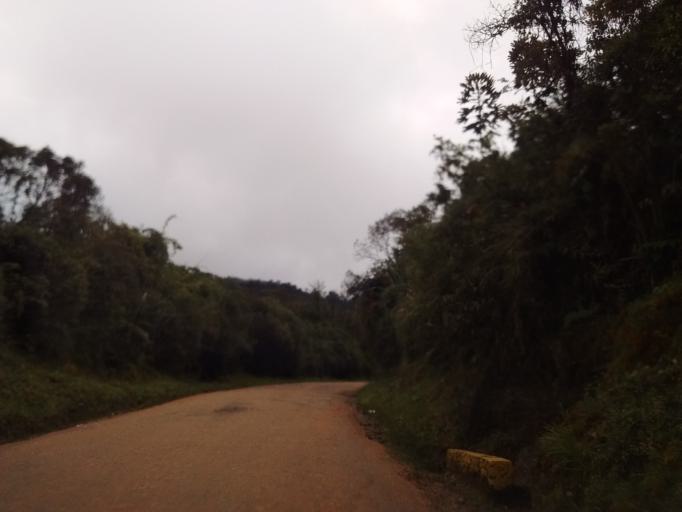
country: CO
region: Huila
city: Isnos
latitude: 2.1319
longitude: -76.3796
